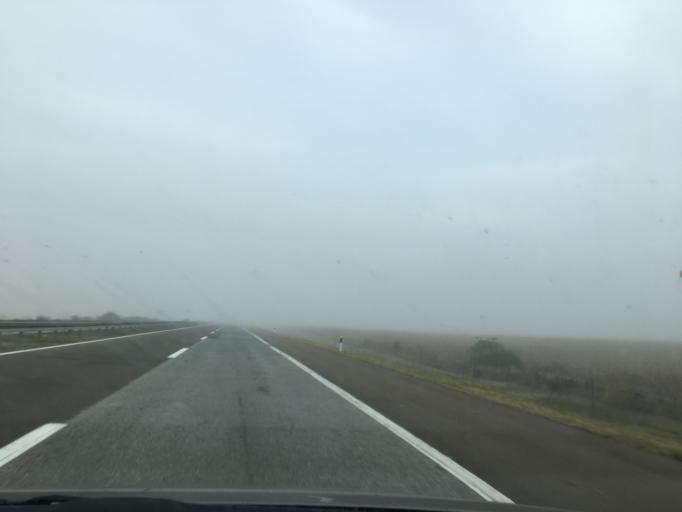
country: RS
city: Novi Karlovci
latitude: 45.0819
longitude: 20.1365
